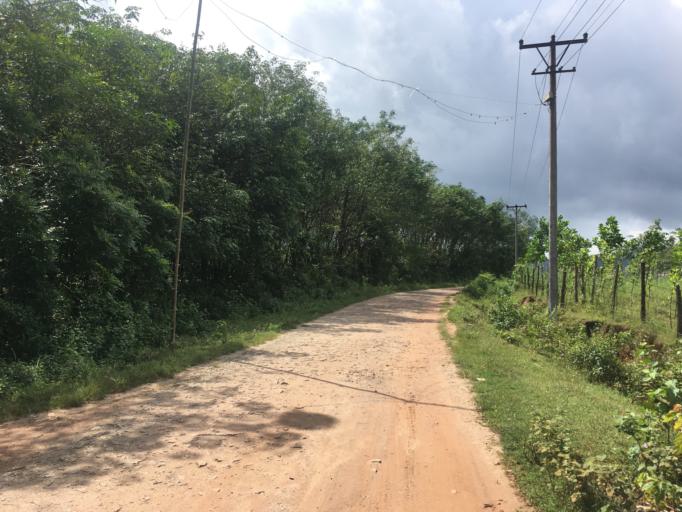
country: MM
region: Mon
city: Mawlamyine
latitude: 16.4632
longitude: 97.6904
